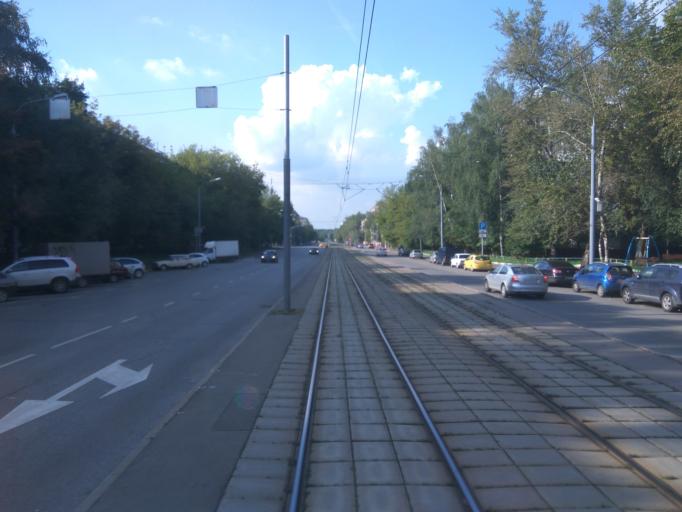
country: RU
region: Moscow
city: Perovo
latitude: 55.7569
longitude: 37.7890
